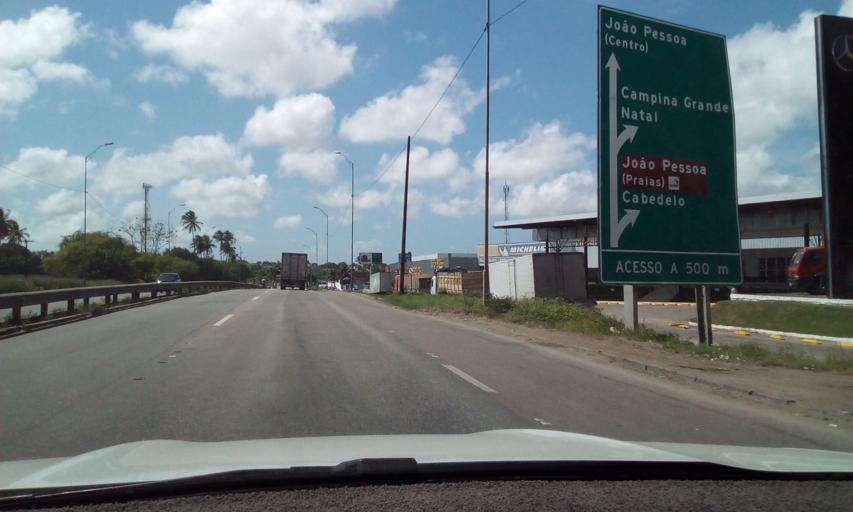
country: BR
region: Paraiba
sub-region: Bayeux
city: Bayeux
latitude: -7.1722
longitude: -34.8979
